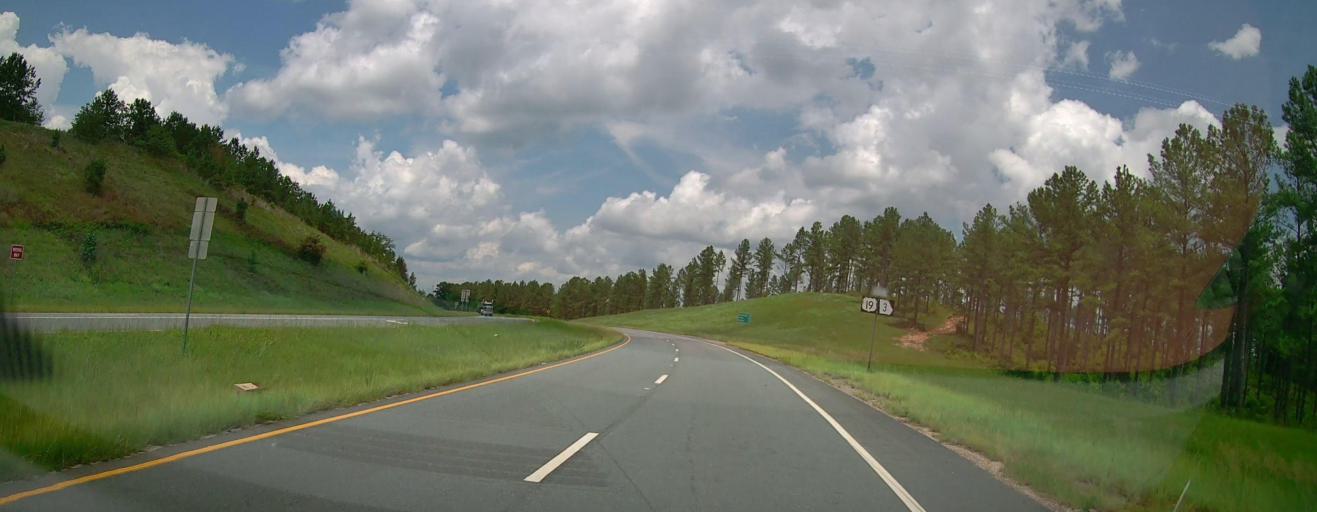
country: US
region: Georgia
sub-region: Taylor County
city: Butler
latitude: 32.7371
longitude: -84.2192
